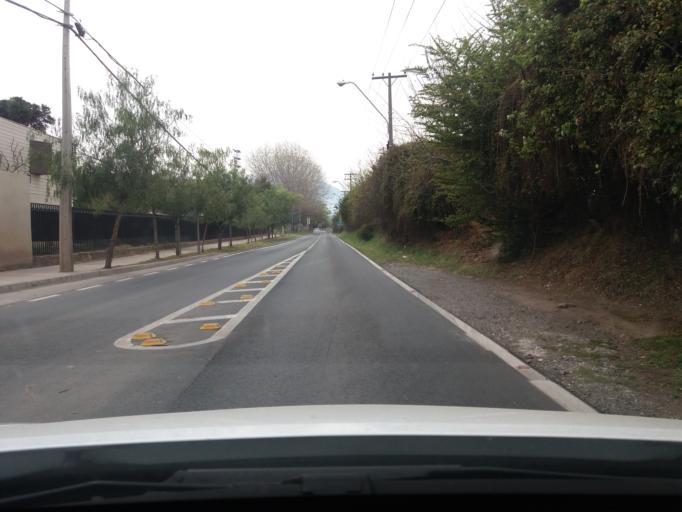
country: CL
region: Valparaiso
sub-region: Provincia de Los Andes
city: Los Andes
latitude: -32.8319
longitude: -70.6211
